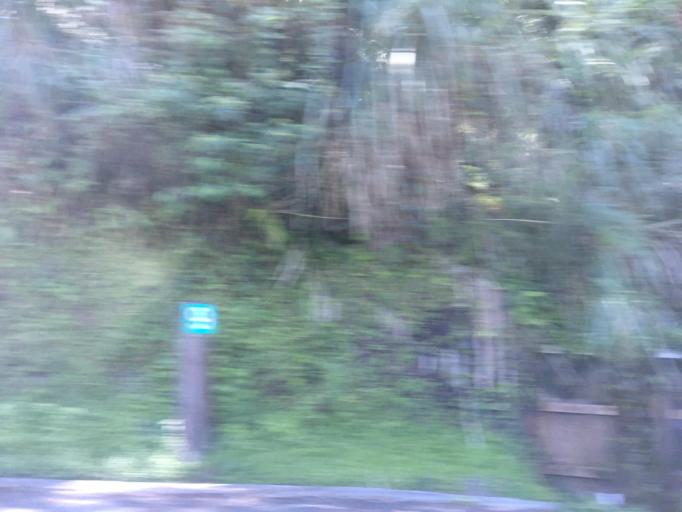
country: TW
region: Taiwan
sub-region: Yilan
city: Yilan
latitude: 24.5378
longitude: 121.5175
